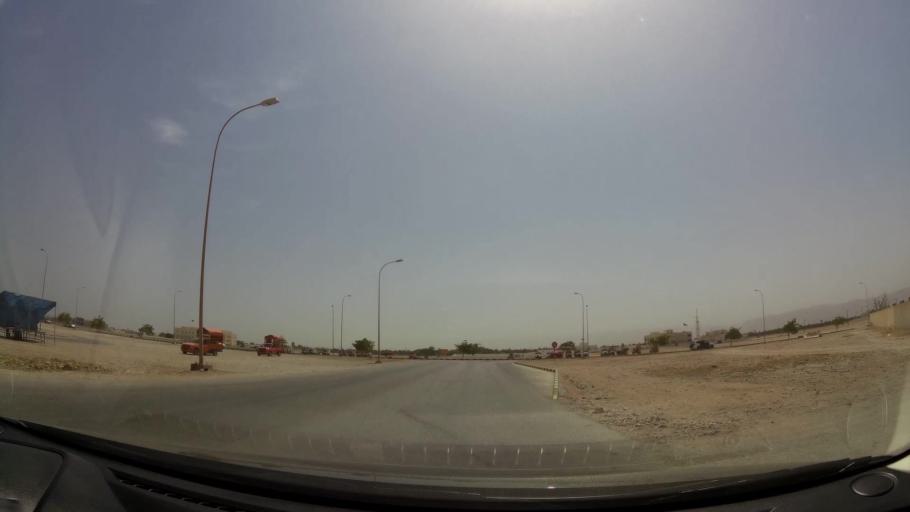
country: OM
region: Zufar
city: Salalah
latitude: 17.0538
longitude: 54.1498
